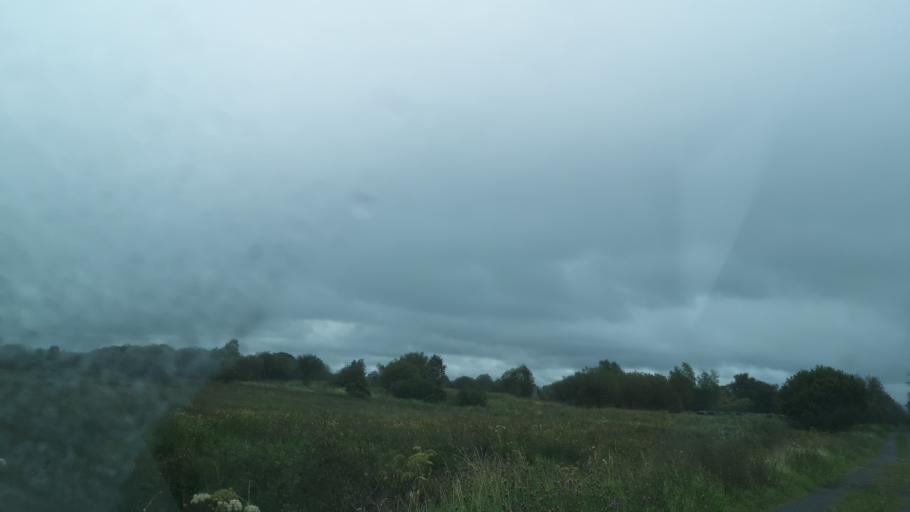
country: IE
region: Connaught
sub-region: County Galway
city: Athenry
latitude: 53.3045
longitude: -8.6458
